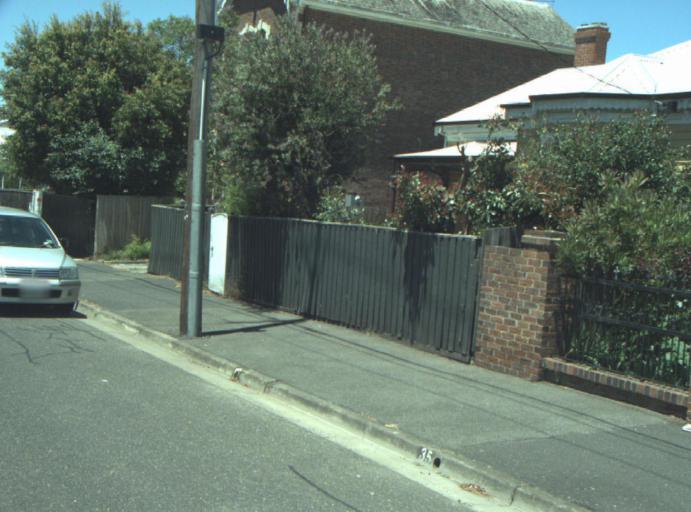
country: AU
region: Victoria
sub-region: Greater Geelong
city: Geelong West
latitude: -38.1490
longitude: 144.3489
